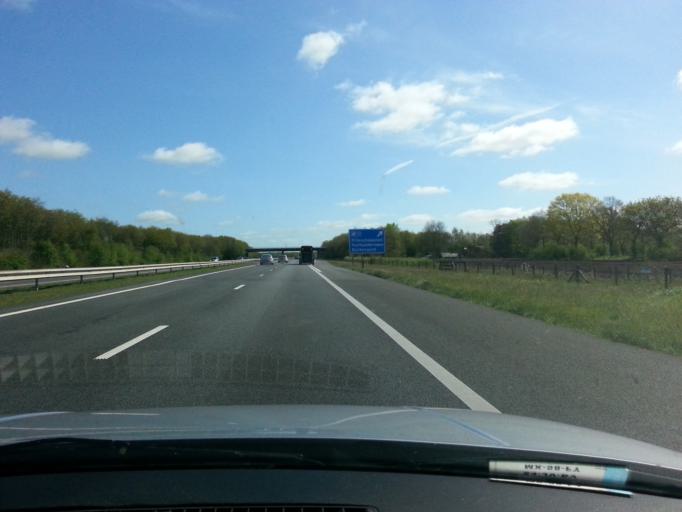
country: NL
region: Friesland
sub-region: Gemeente Smallingerland
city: Drachtstercompagnie
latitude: 53.1277
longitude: 6.1810
